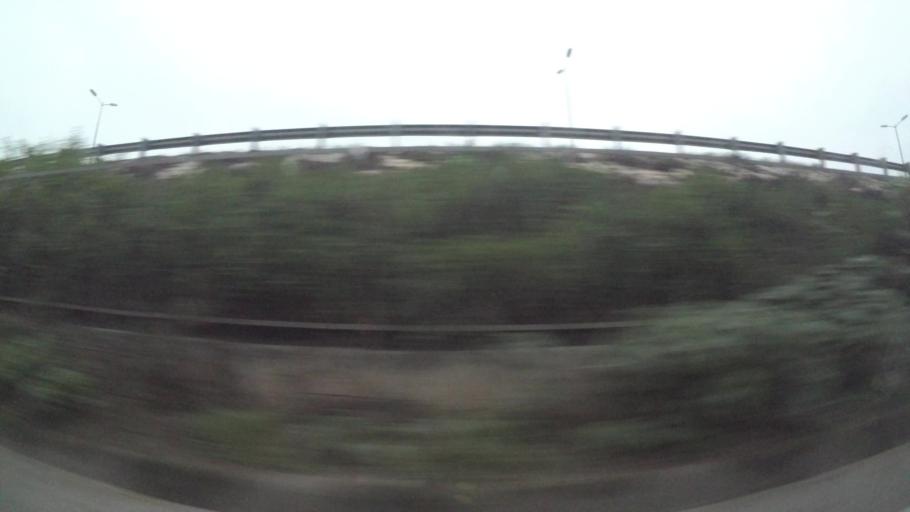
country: VN
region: Ha Noi
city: Van Dien
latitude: 20.9754
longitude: 105.8855
